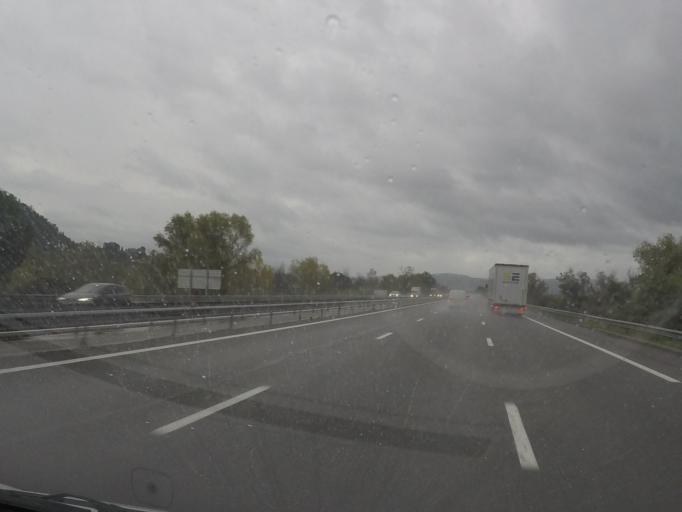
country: FR
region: Provence-Alpes-Cote d'Azur
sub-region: Departement du Var
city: Vidauban
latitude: 43.4025
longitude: 6.3961
